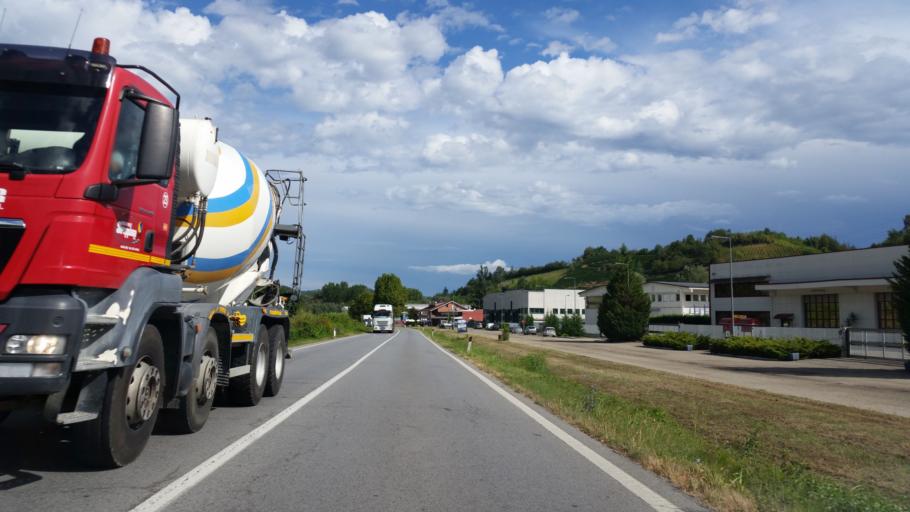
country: IT
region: Piedmont
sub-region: Provincia di Cuneo
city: Vezza d'Alba
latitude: 44.7743
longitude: 8.0079
